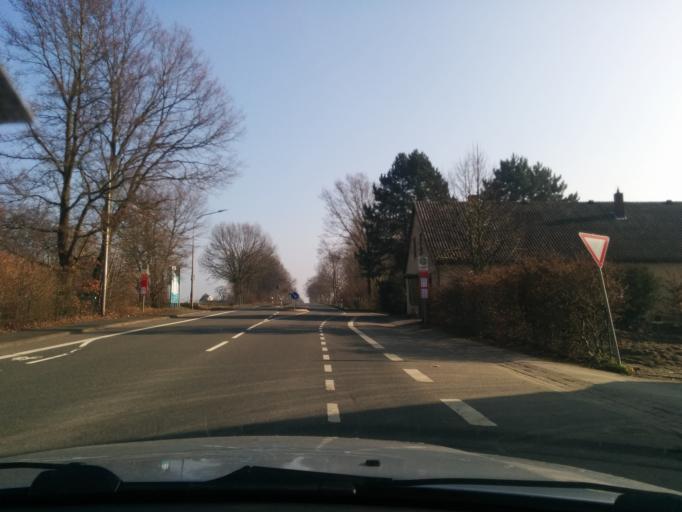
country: DE
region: North Rhine-Westphalia
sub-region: Regierungsbezirk Detmold
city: Lemgo
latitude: 52.0148
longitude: 8.9298
